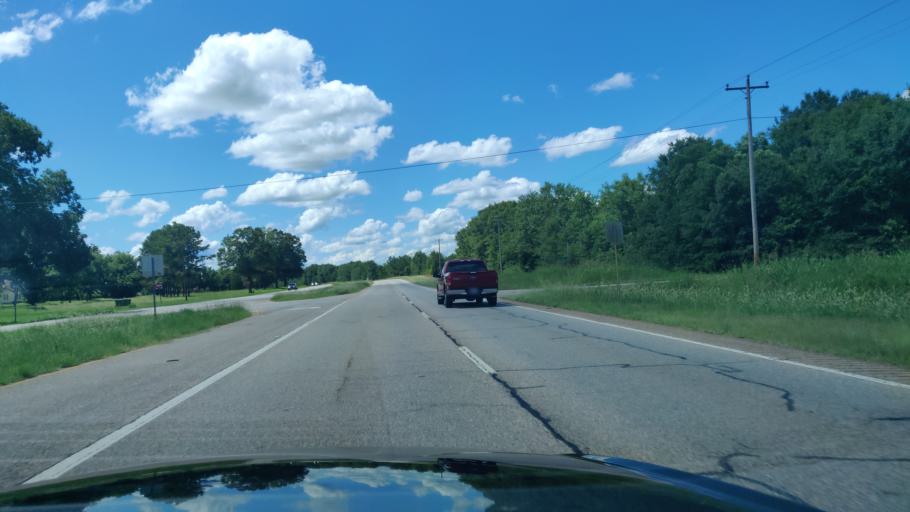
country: US
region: Georgia
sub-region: Stewart County
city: Richland
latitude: 32.0043
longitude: -84.6490
